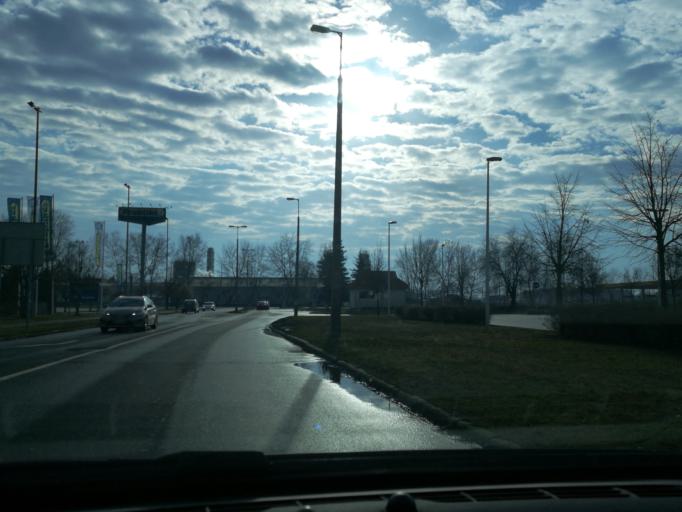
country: HU
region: Szabolcs-Szatmar-Bereg
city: Nyiregyhaza
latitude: 47.9535
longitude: 21.7437
